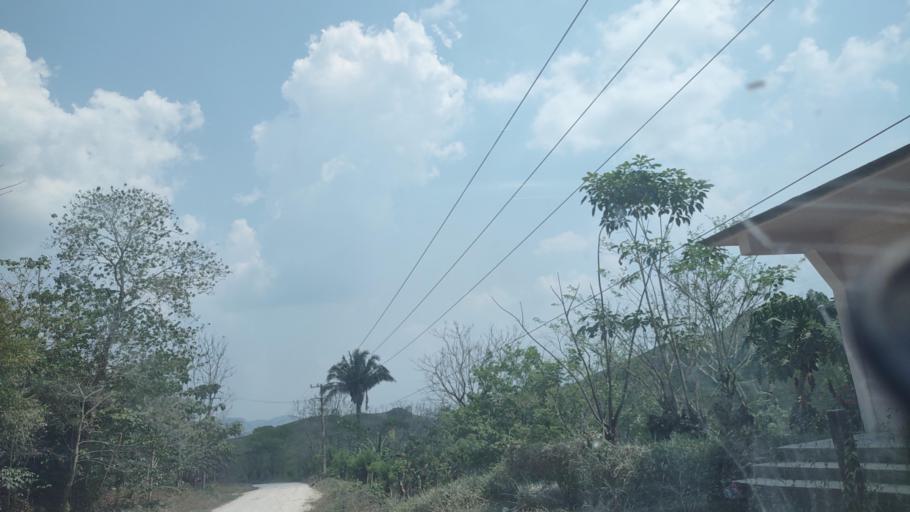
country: MX
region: Tabasco
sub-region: Huimanguillo
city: Francisco Rueda
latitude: 17.6031
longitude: -93.9051
